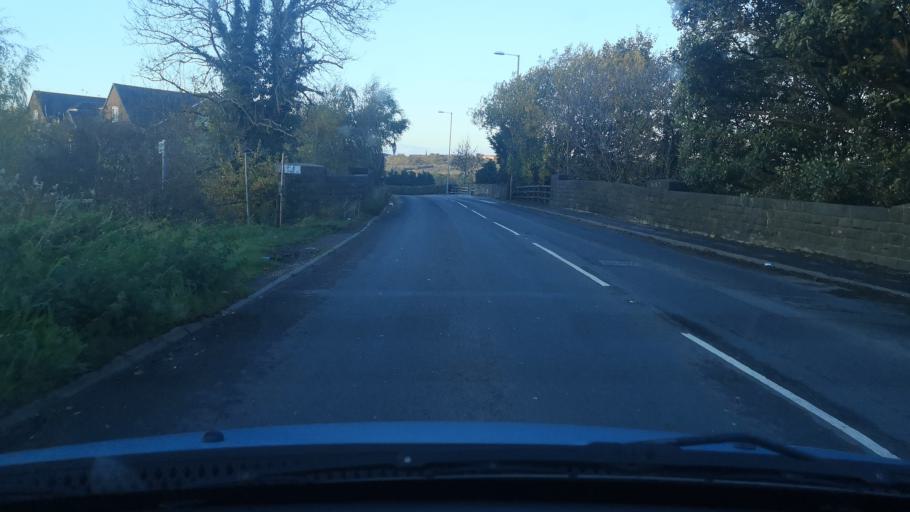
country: GB
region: England
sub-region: City and Borough of Wakefield
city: Horbury
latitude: 53.6536
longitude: -1.5748
